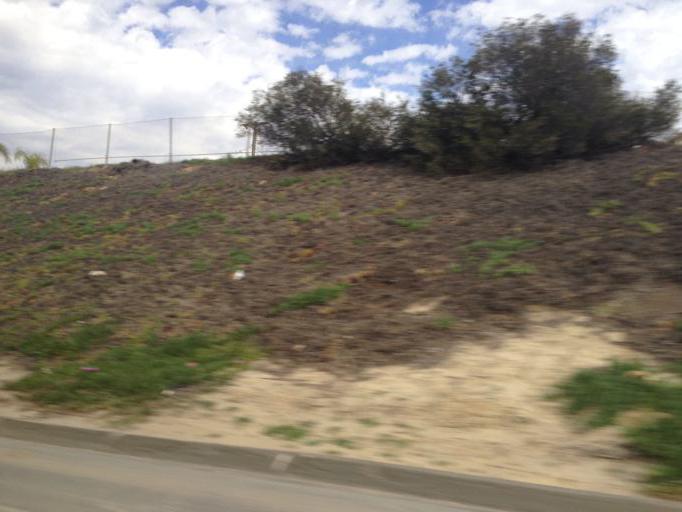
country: US
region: California
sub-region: San Diego County
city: Bonita
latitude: 32.6236
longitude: -117.0412
